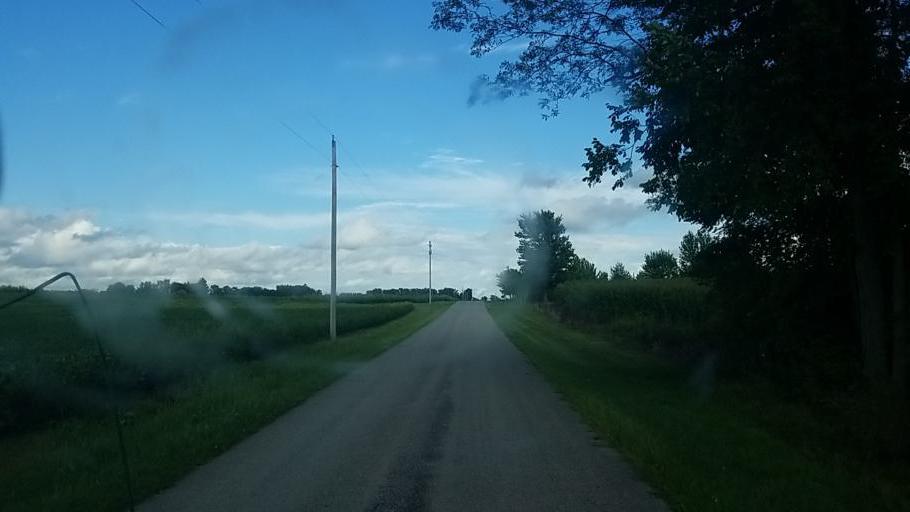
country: US
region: Ohio
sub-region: Hardin County
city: Forest
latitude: 40.7887
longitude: -83.4277
